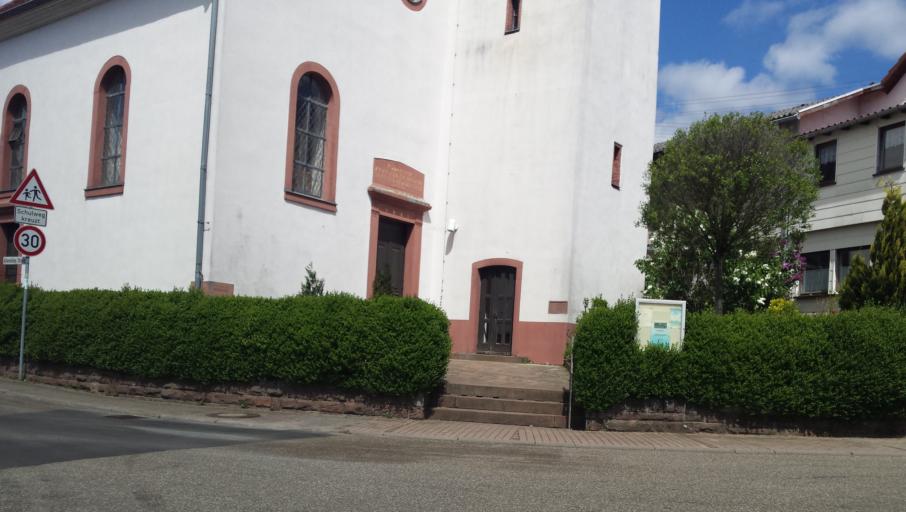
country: DE
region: Baden-Wuerttemberg
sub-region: Karlsruhe Region
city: Neunkirchen
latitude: 49.4018
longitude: 8.9745
